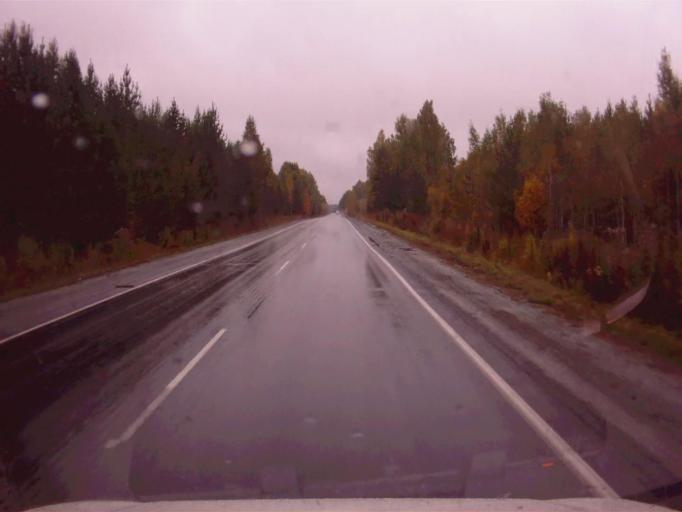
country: RU
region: Chelyabinsk
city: Tayginka
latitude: 55.5411
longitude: 60.6466
